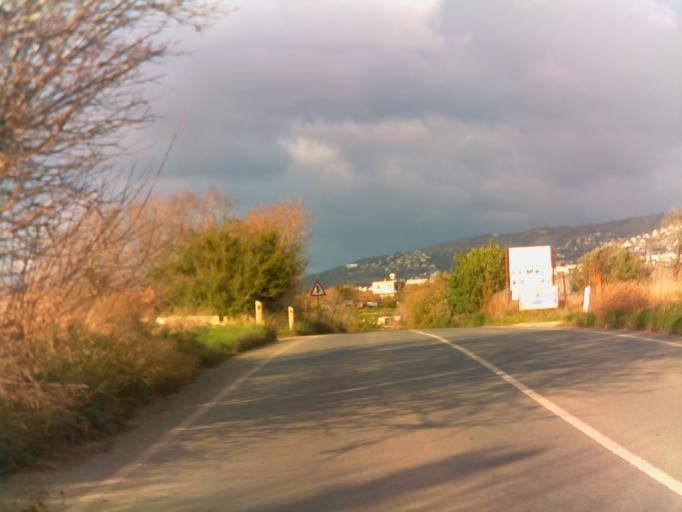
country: CY
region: Pafos
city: Kissonerga
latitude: 34.8170
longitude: 32.4122
